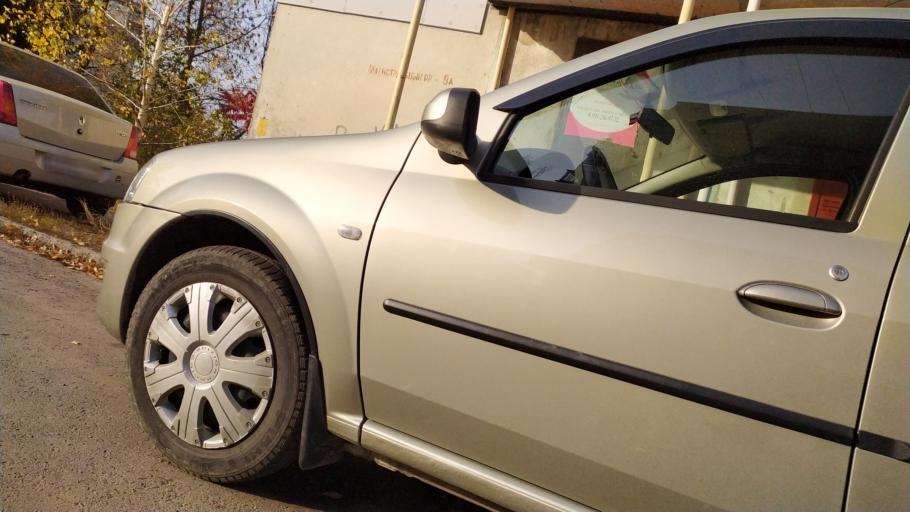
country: RU
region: Kursk
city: Kursk
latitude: 51.6480
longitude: 36.1394
